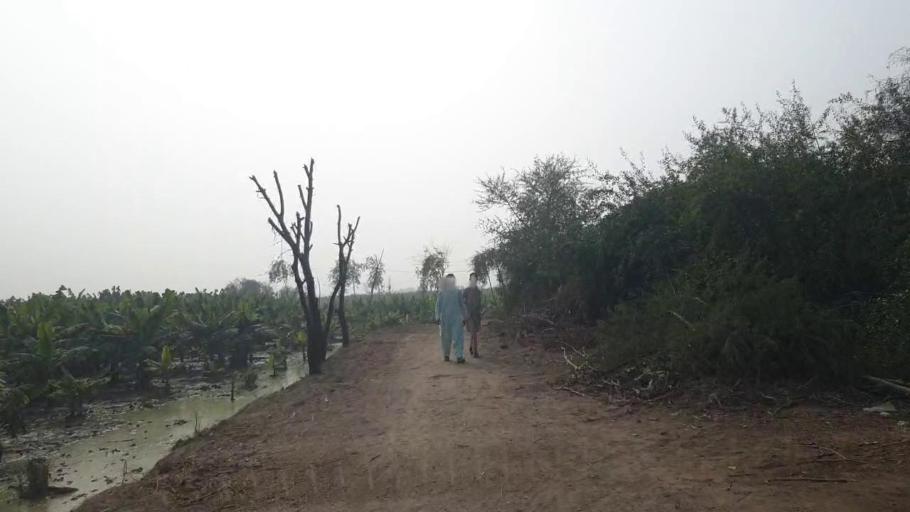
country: PK
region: Sindh
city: Bhit Shah
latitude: 25.7710
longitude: 68.5736
